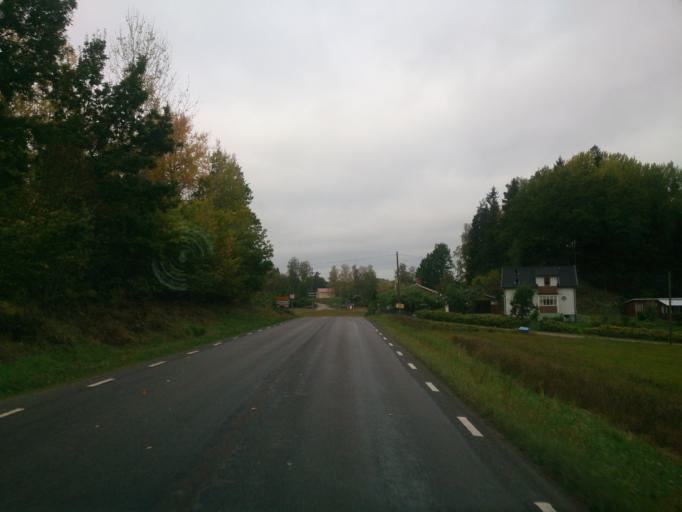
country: SE
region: OEstergoetland
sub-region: Atvidabergs Kommun
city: Atvidaberg
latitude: 58.1809
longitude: 16.0588
